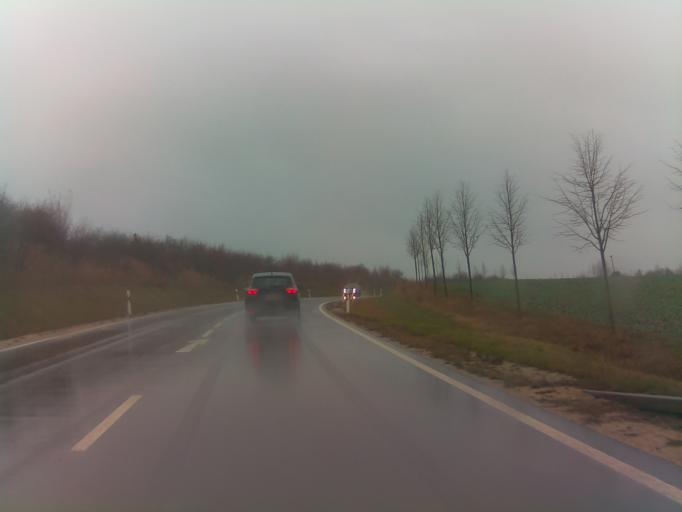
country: DE
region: Thuringia
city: Eisfeld
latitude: 50.4292
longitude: 10.8926
